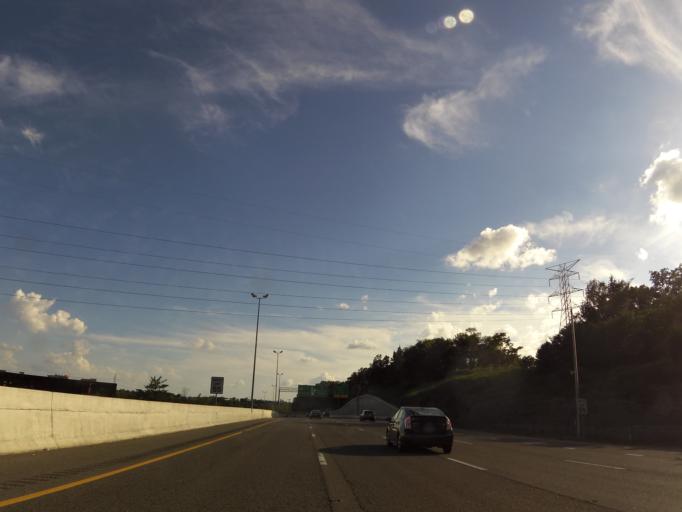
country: US
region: Tennessee
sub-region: Davidson County
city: Nashville
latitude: 36.1630
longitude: -86.6901
